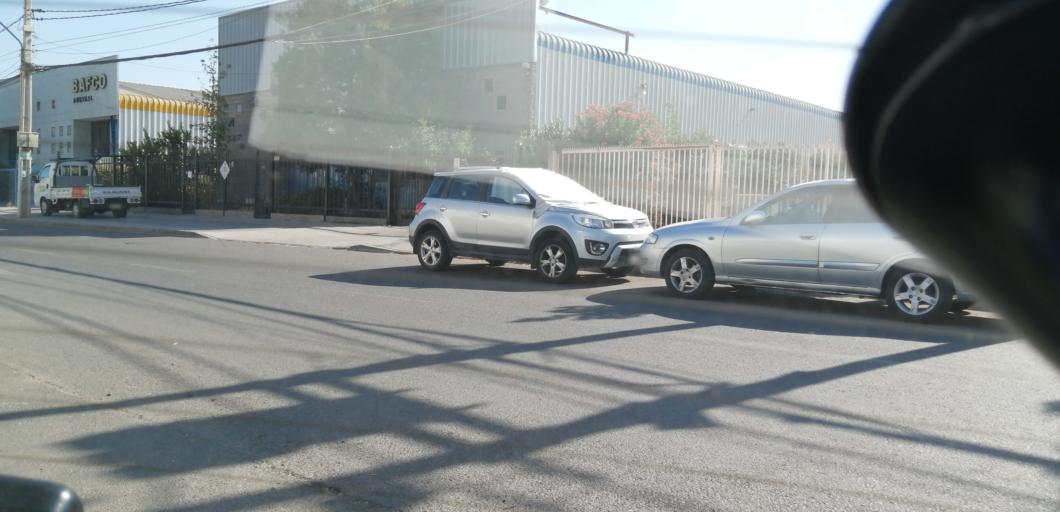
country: CL
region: Santiago Metropolitan
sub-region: Provincia de Santiago
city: Lo Prado
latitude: -33.3824
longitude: -70.7778
